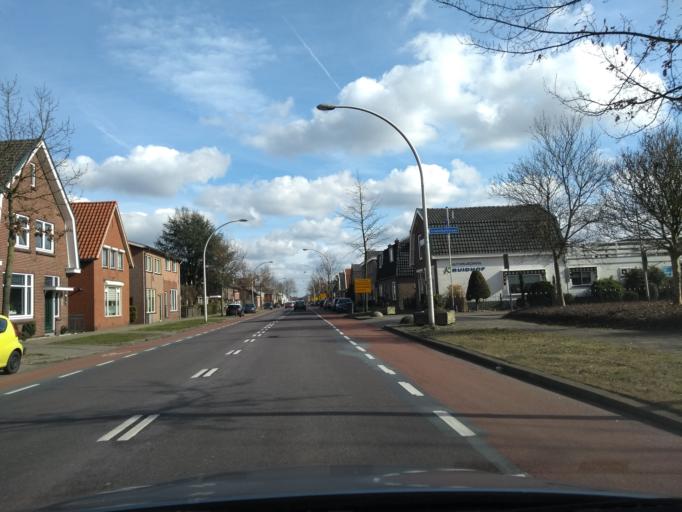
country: NL
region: Overijssel
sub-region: Gemeente Hengelo
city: Hengelo
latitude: 52.2527
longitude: 6.7835
